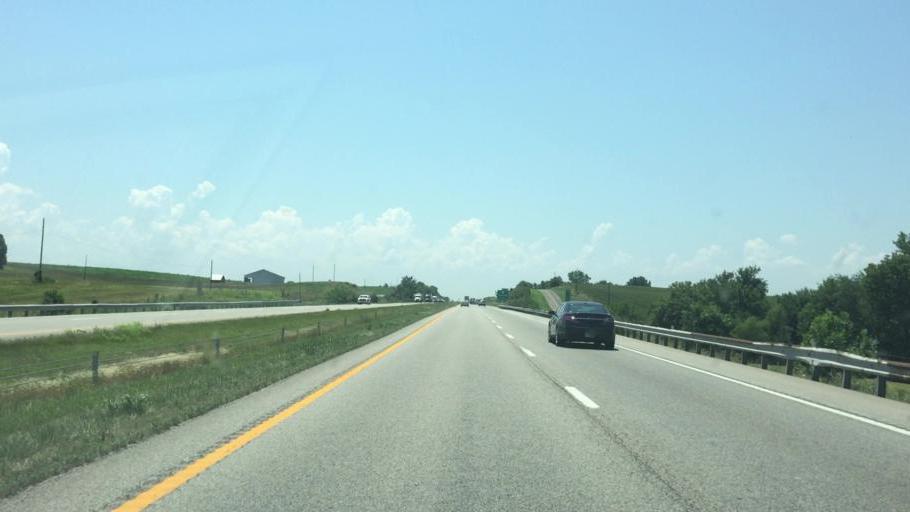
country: US
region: Kansas
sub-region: Doniphan County
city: Elwood
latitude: 39.6189
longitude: -94.7884
